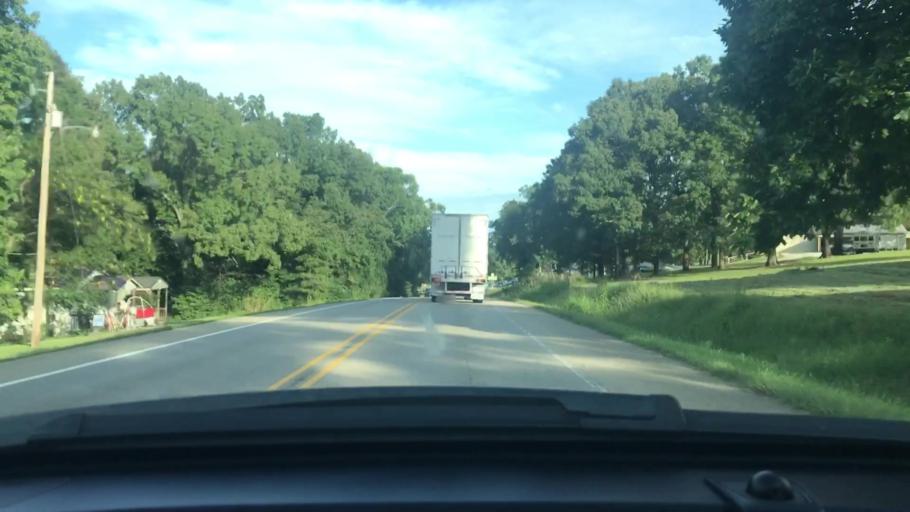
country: US
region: Arkansas
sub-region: Sharp County
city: Cherokee Village
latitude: 36.2386
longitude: -91.2586
